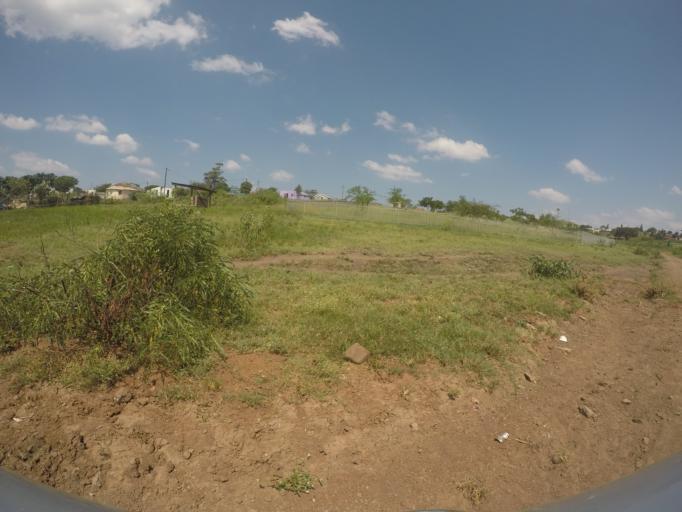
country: ZA
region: KwaZulu-Natal
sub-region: uThungulu District Municipality
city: Empangeni
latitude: -28.5895
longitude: 31.7406
